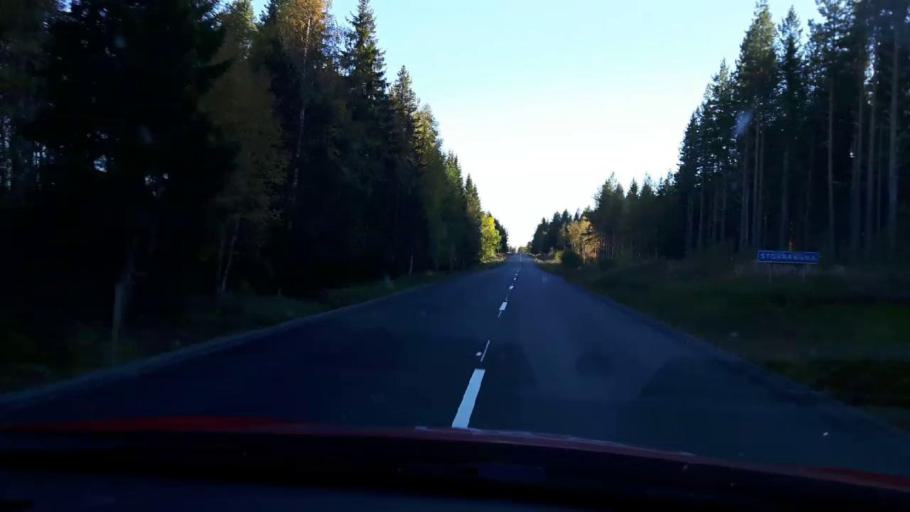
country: SE
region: Jaemtland
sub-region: OEstersunds Kommun
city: Lit
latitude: 63.5391
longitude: 14.8501
